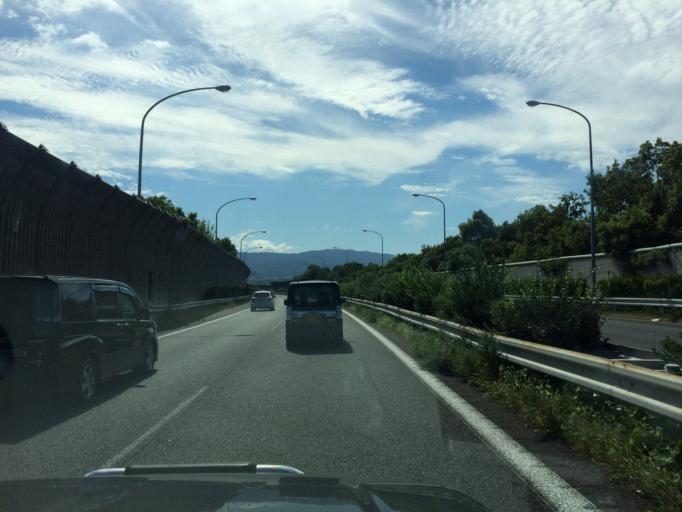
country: JP
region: Osaka
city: Izumi
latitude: 34.4747
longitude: 135.4632
